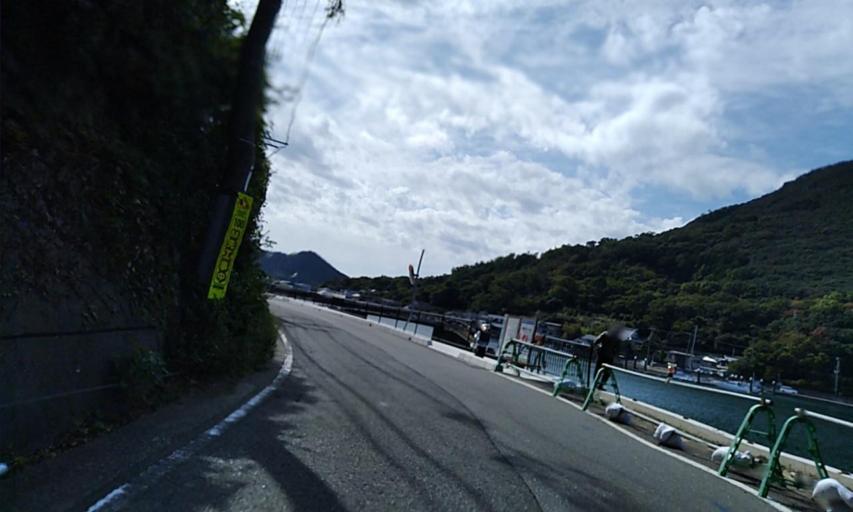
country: JP
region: Wakayama
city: Gobo
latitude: 33.9649
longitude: 135.1021
